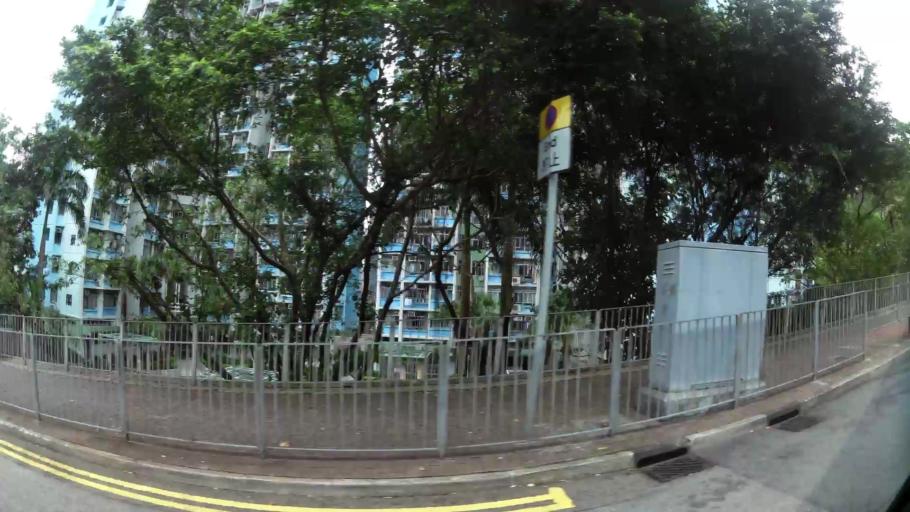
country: HK
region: Wanchai
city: Wan Chai
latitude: 22.2797
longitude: 114.2180
